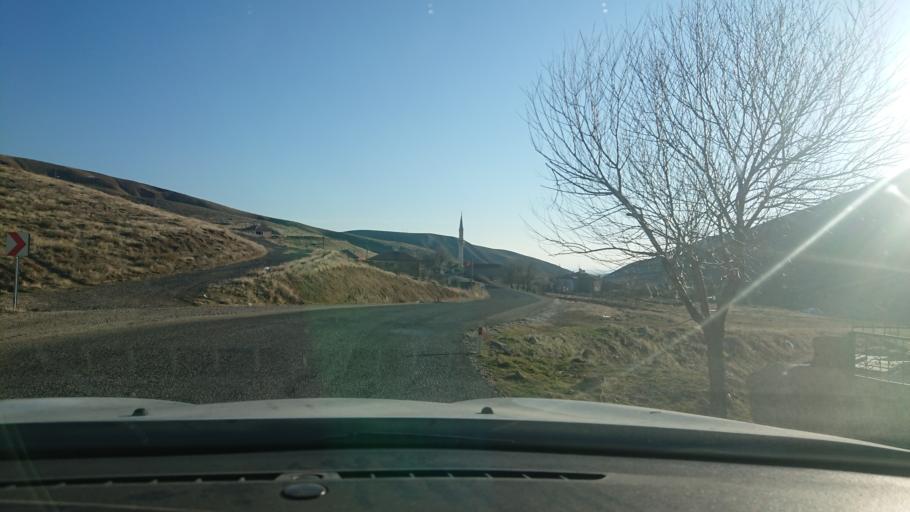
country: TR
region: Aksaray
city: Acipinar
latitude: 38.6942
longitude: 33.7482
